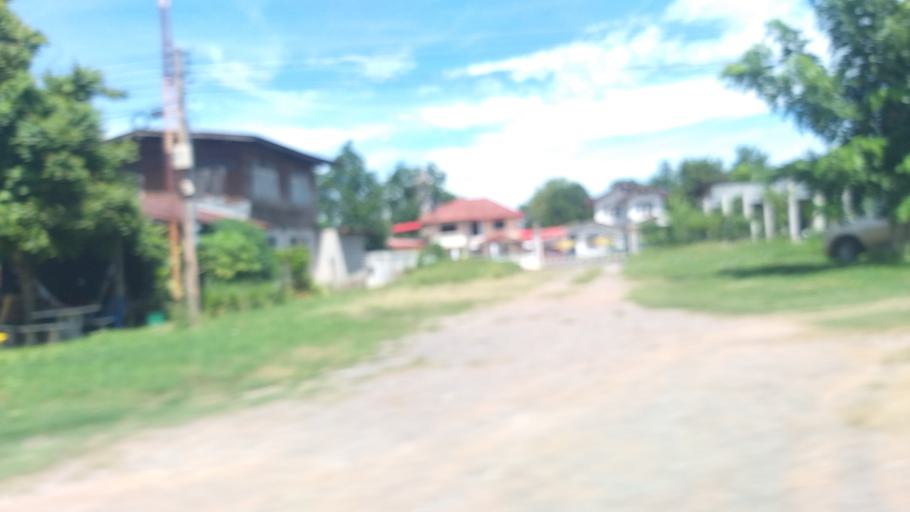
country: TH
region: Khon Kaen
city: Nong Ruea
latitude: 16.4670
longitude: 102.4418
